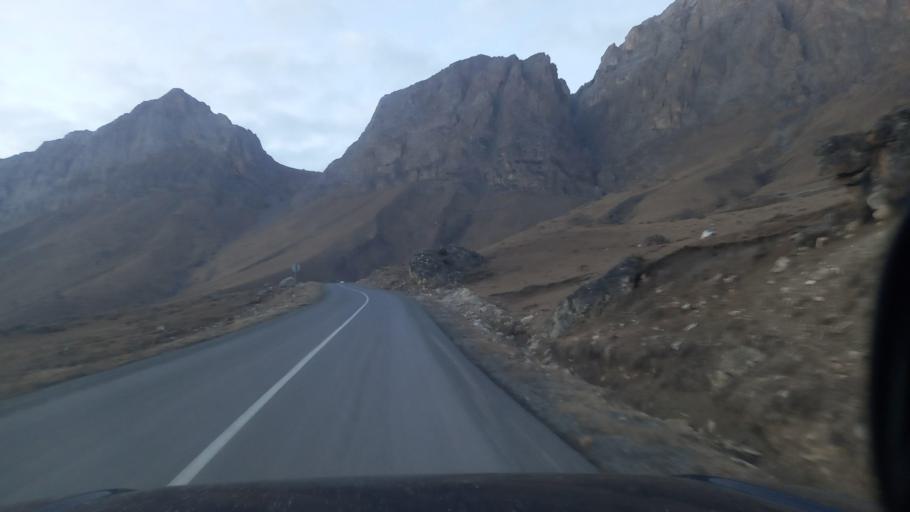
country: RU
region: Ingushetiya
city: Dzhayrakh
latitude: 42.8212
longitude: 44.8267
